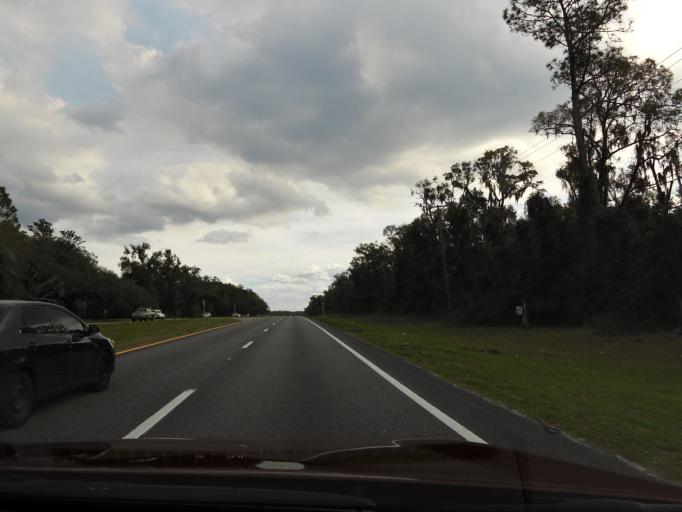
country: US
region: Florida
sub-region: Volusia County
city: De Leon Springs
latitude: 29.1094
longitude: -81.3471
